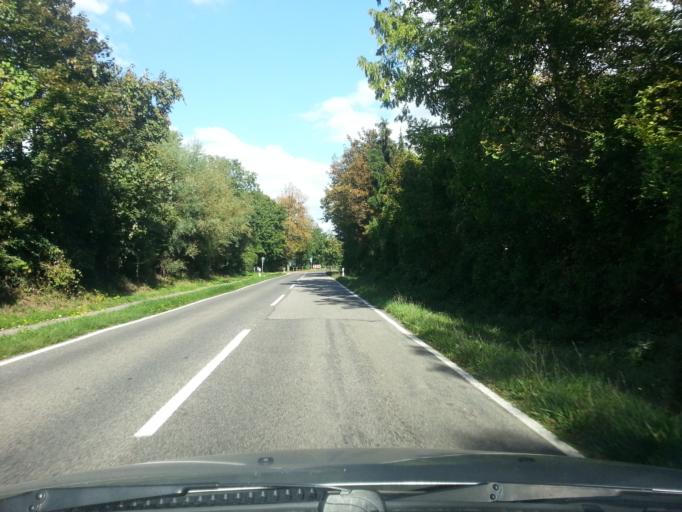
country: DE
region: Rheinland-Pfalz
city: Germersheim
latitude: 49.2294
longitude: 8.4009
